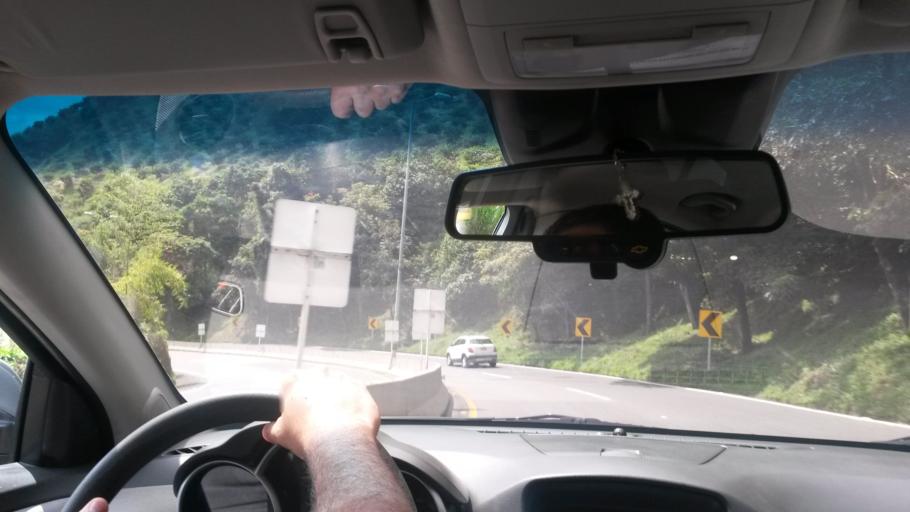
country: CO
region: Caldas
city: Palestina
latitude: 5.0455
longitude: -75.5777
